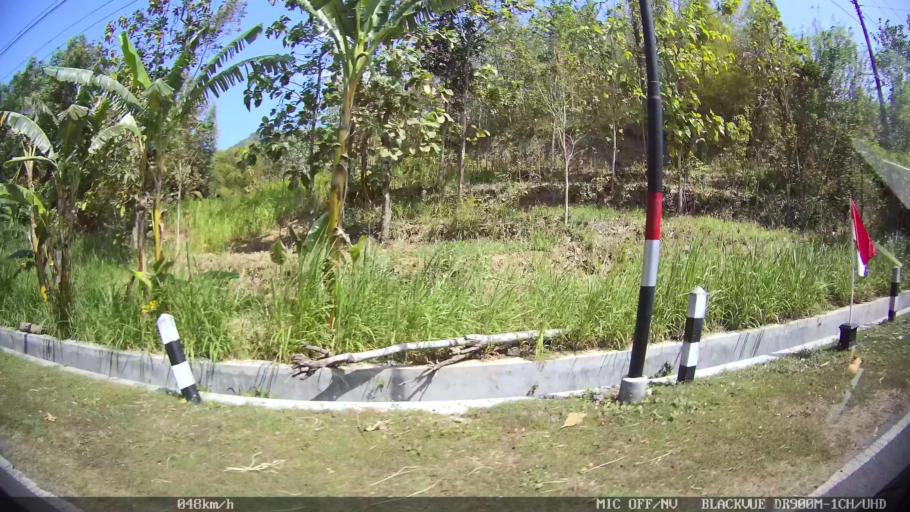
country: ID
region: Daerah Istimewa Yogyakarta
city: Pundong
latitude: -7.9871
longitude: 110.3251
